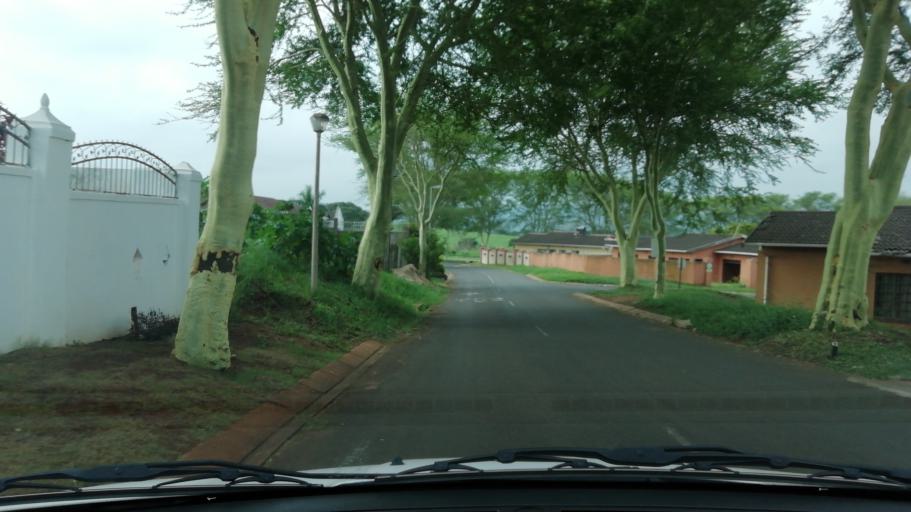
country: ZA
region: KwaZulu-Natal
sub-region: uThungulu District Municipality
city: Empangeni
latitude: -28.7370
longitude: 31.8770
